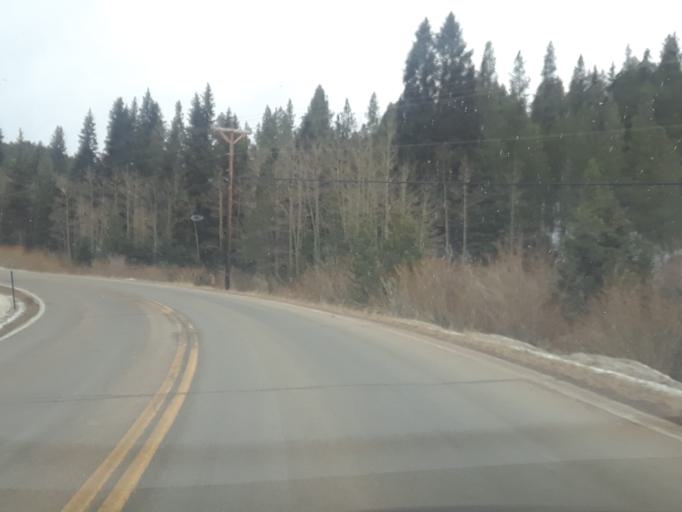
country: US
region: Colorado
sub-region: Boulder County
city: Coal Creek
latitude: 39.8254
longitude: -105.4109
